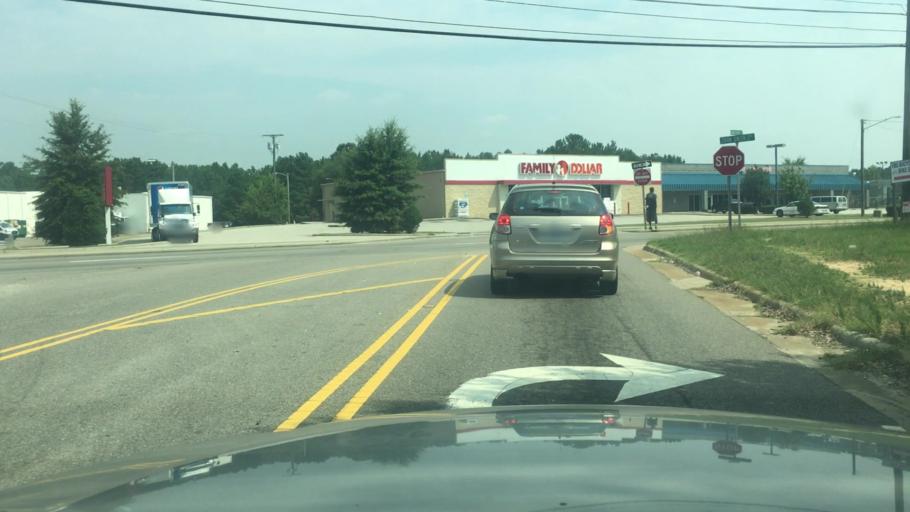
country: US
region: North Carolina
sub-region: Cumberland County
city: Hope Mills
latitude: 35.0061
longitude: -78.9648
